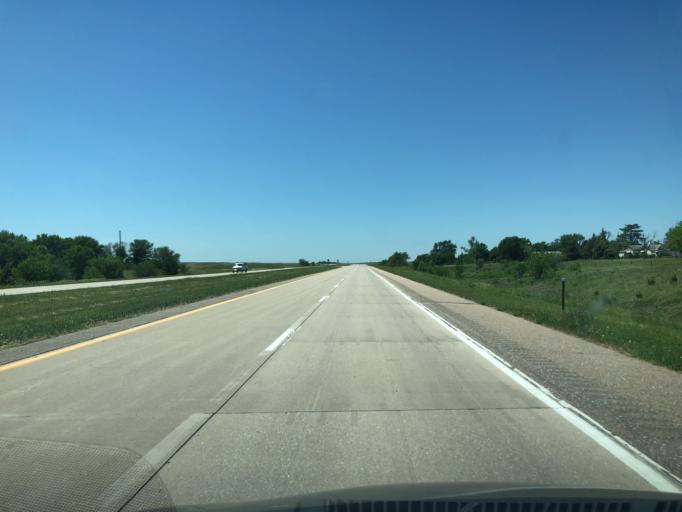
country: US
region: Nebraska
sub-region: Thayer County
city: Hebron
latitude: 40.1346
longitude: -97.6036
